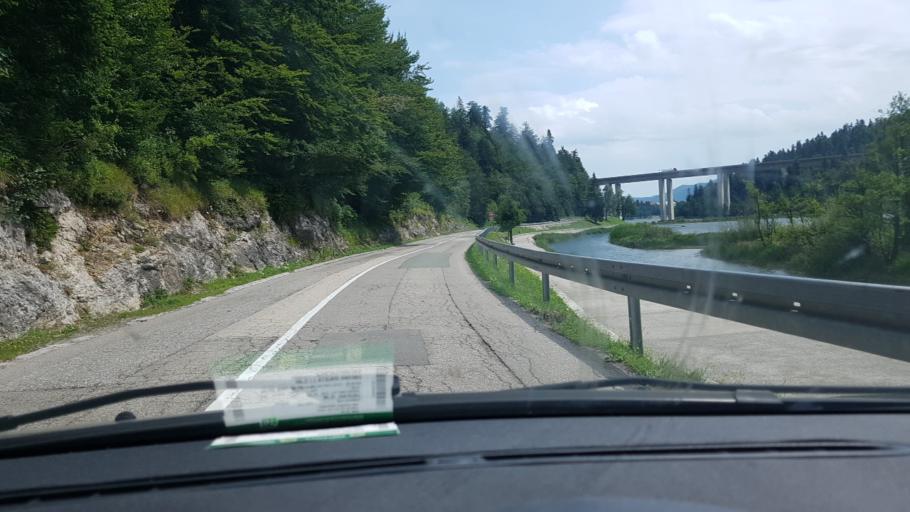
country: HR
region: Primorsko-Goranska
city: Hreljin
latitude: 45.3223
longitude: 14.7068
